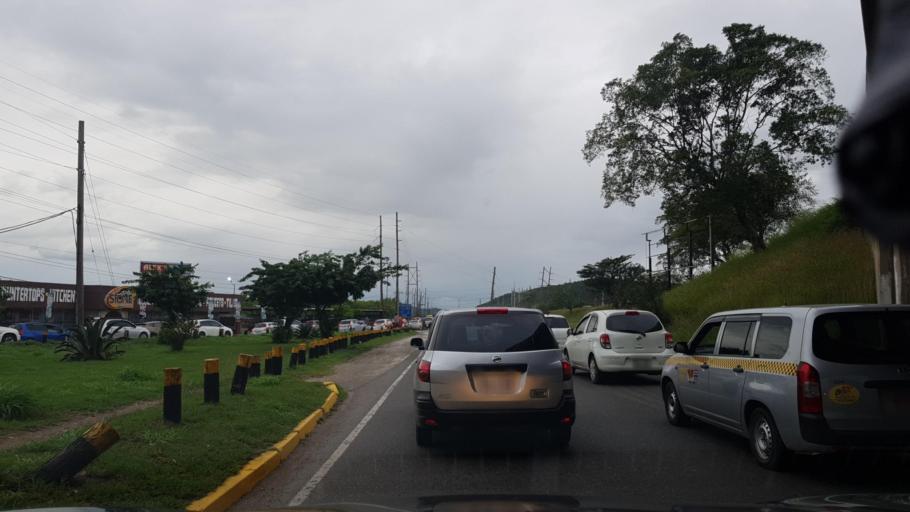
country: JM
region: Saint Andrew
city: Half Way Tree
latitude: 18.0259
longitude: -76.8551
